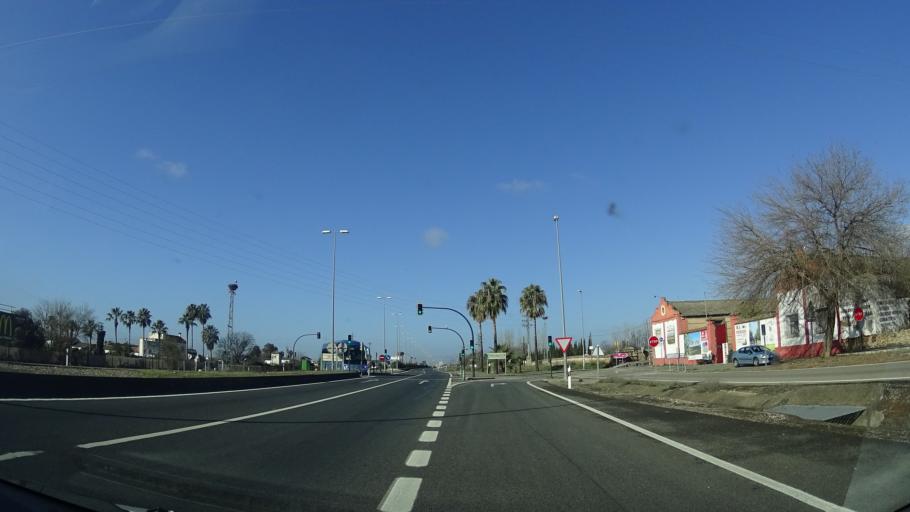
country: ES
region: Andalusia
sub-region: Province of Cordoba
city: Villarrubia
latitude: 37.8759
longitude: -4.8481
